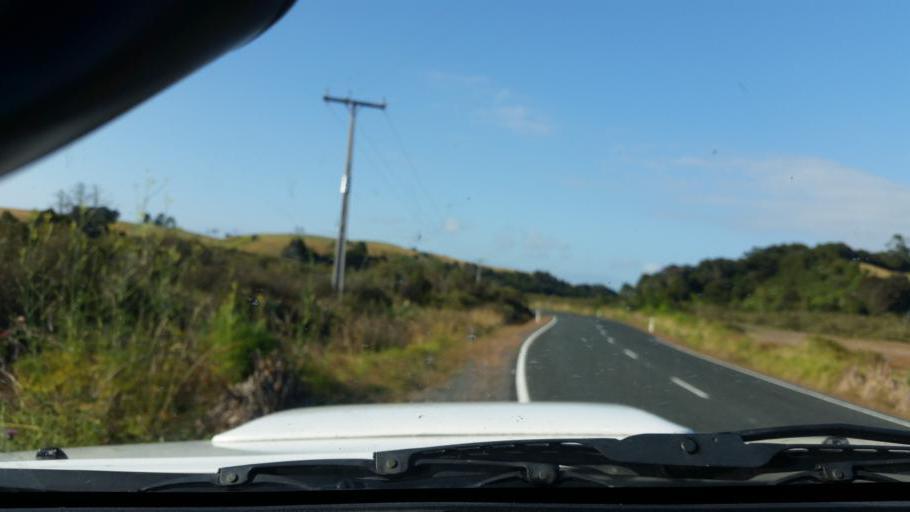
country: NZ
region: Northland
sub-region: Whangarei
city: Ruakaka
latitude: -36.1122
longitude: 174.2300
